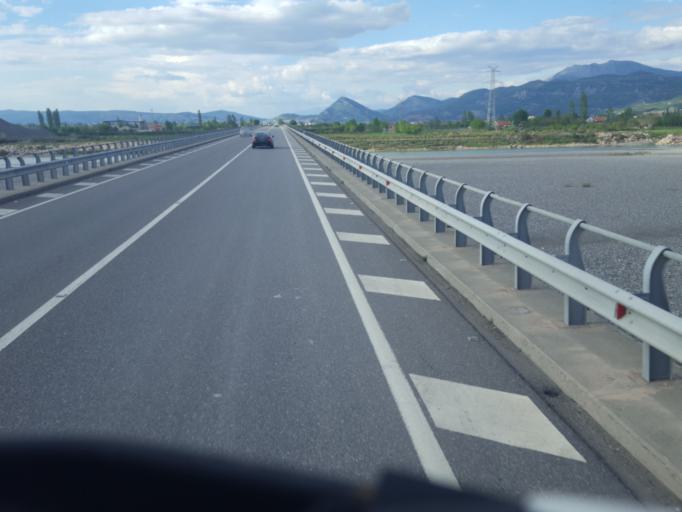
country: AL
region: Lezhe
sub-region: Rrethi i Lezhes
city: Shenkoll
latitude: 41.6834
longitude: 19.6722
